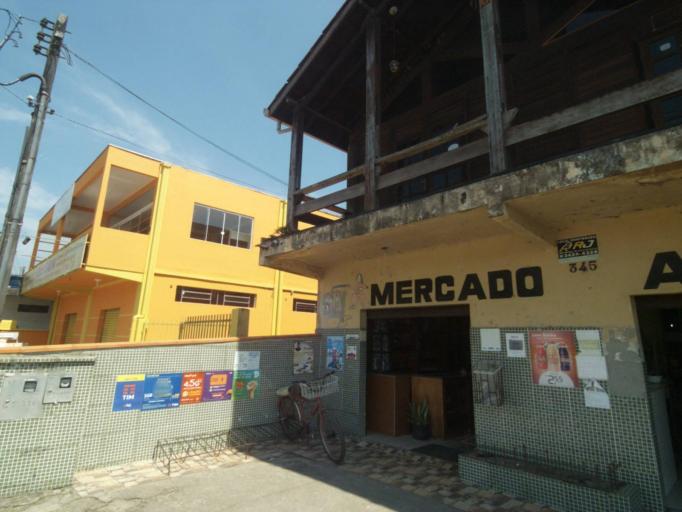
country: BR
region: Parana
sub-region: Paranagua
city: Paranagua
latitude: -25.5536
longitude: -48.6274
